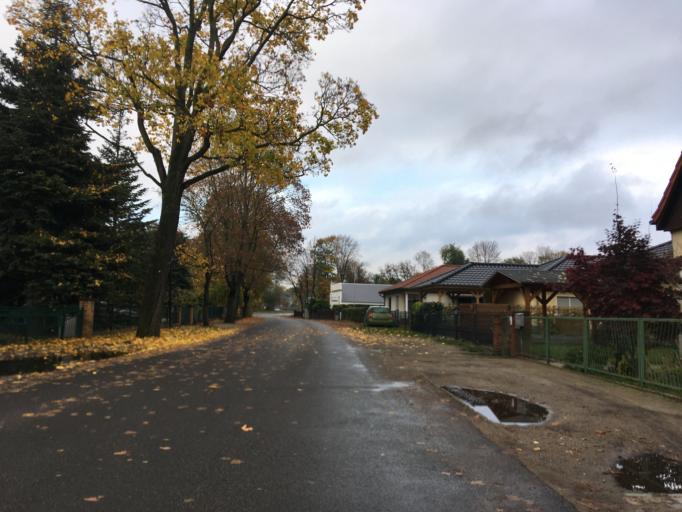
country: DE
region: Brandenburg
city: Furstenwalde
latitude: 52.3519
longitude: 14.0627
